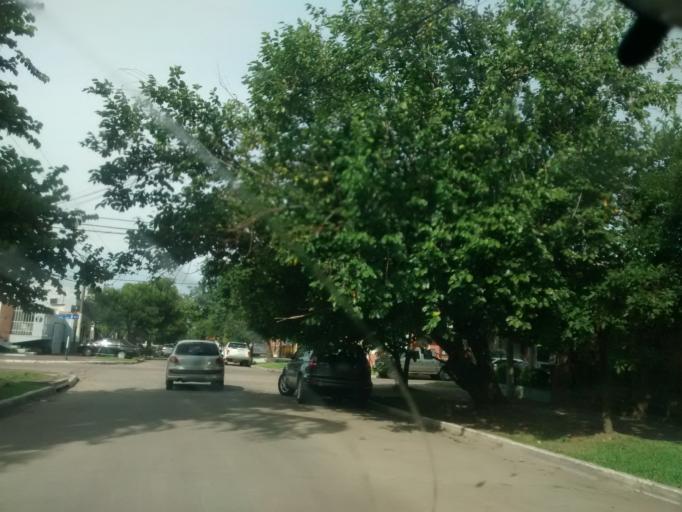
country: AR
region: Chaco
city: Resistencia
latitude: -27.4433
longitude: -58.9993
